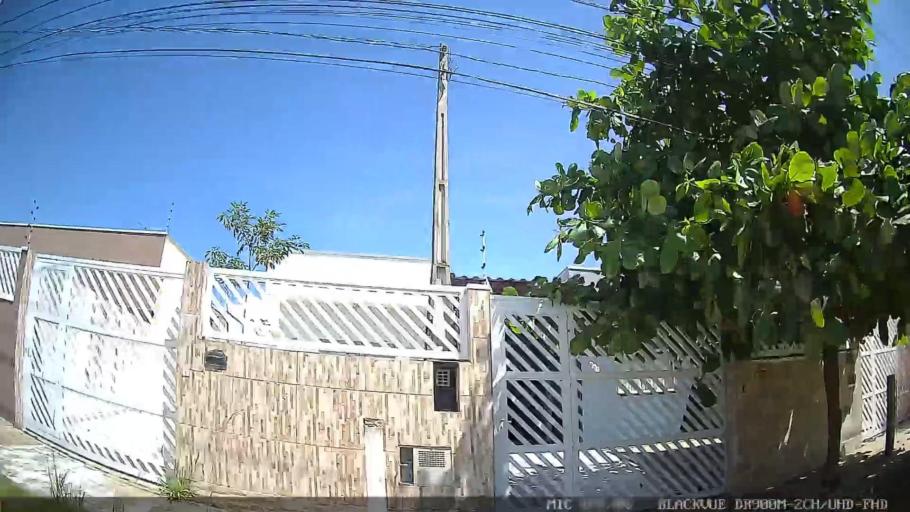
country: BR
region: Sao Paulo
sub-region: Peruibe
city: Peruibe
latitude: -24.2979
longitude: -46.9967
